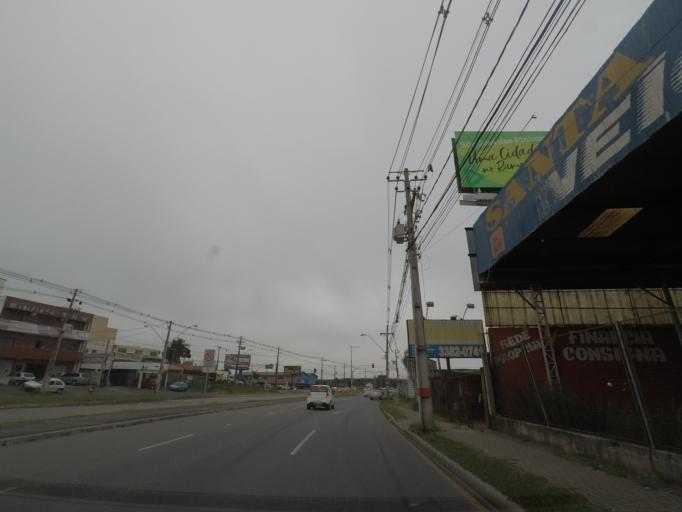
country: BR
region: Parana
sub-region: Sao Jose Dos Pinhais
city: Sao Jose dos Pinhais
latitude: -25.5307
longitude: -49.2154
